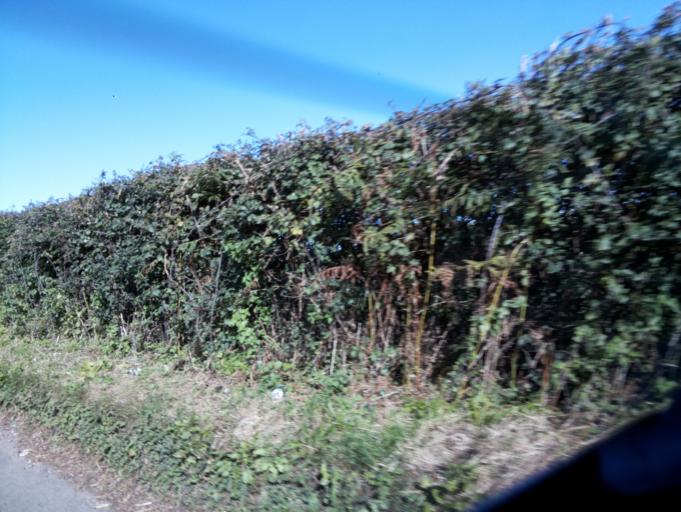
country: GB
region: Wales
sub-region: Torfaen County Borough
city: Cwmbran
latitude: 51.6098
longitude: -3.0489
